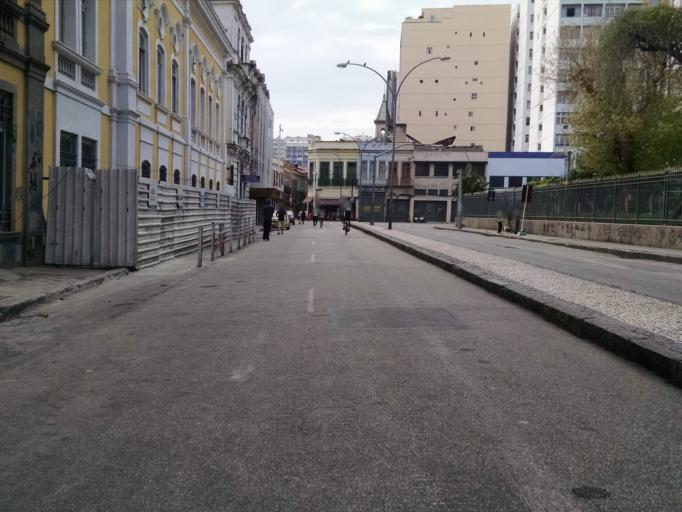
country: BR
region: Rio de Janeiro
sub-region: Rio De Janeiro
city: Rio de Janeiro
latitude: -22.9075
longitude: -43.1865
